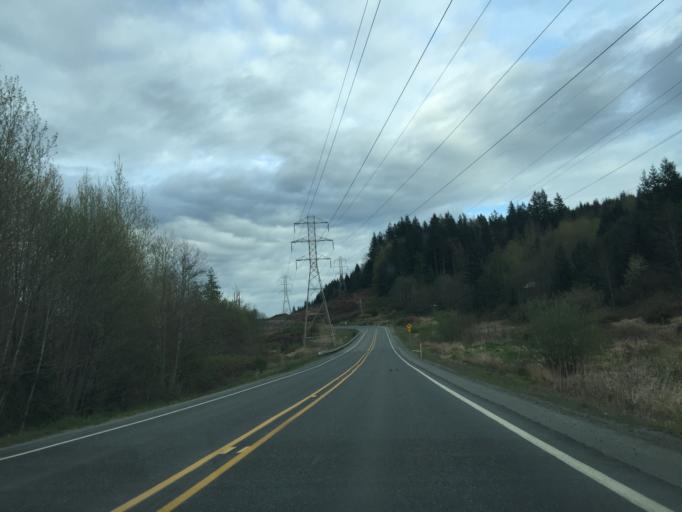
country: US
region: Washington
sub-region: Snohomish County
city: Arlington Heights
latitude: 48.2711
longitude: -121.8628
